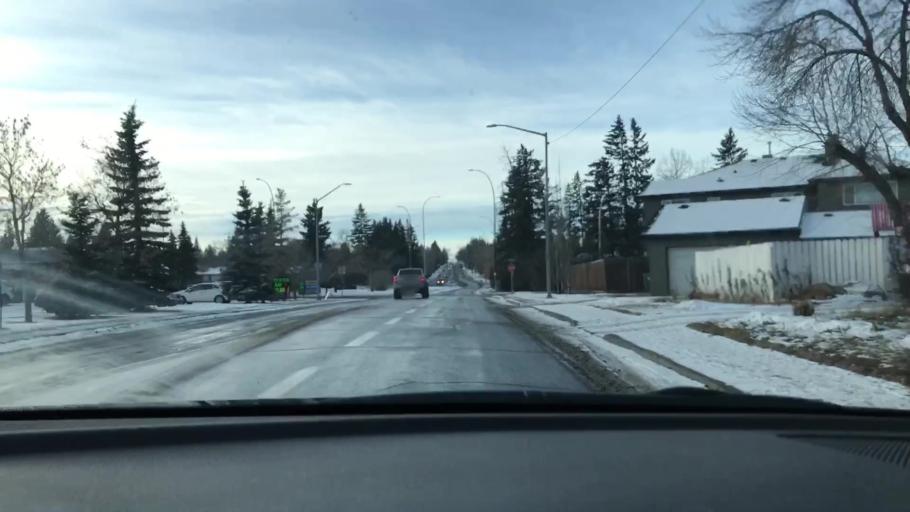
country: CA
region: Alberta
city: Calgary
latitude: 51.0264
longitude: -114.1280
